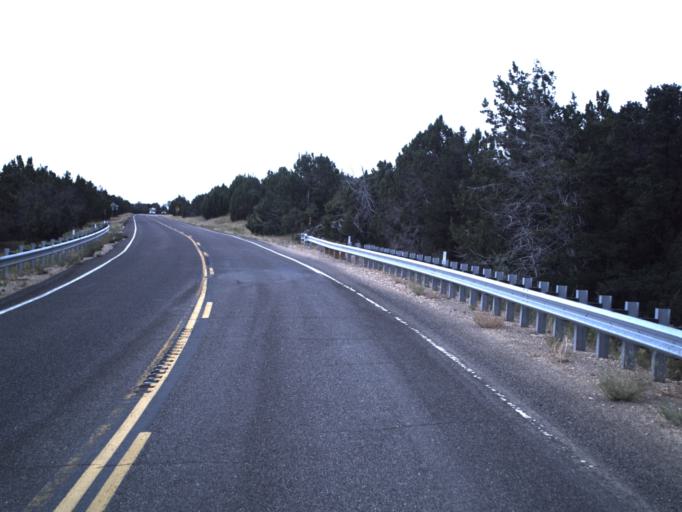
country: US
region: Utah
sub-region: Washington County
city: Hildale
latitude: 37.2608
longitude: -112.7913
